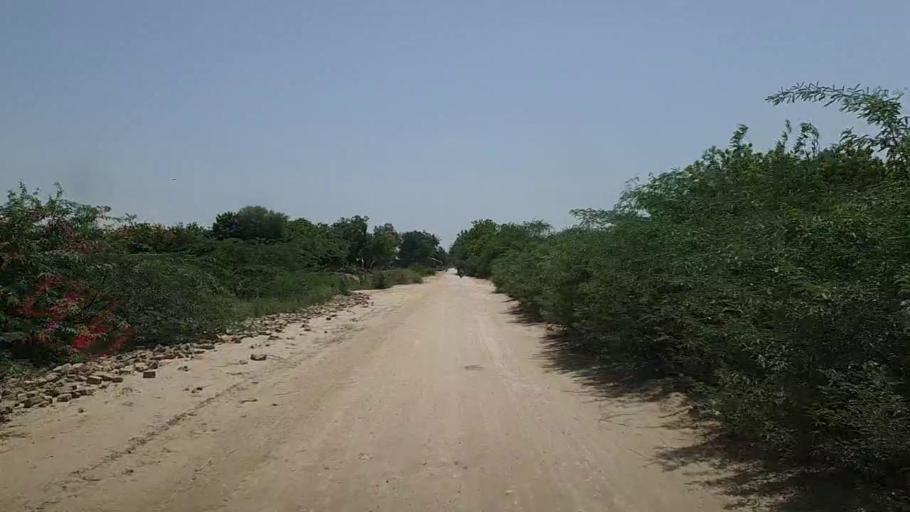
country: PK
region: Sindh
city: Pad Idan
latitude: 26.7593
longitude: 68.2936
